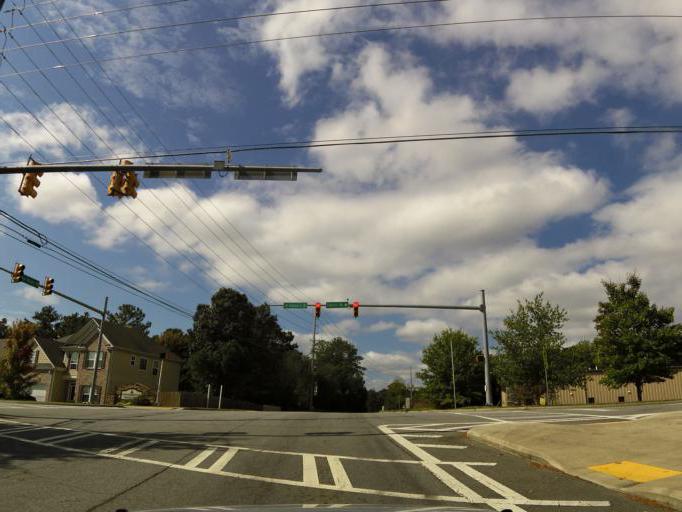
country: US
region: Georgia
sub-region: Cobb County
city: Acworth
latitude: 34.0562
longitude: -84.6536
